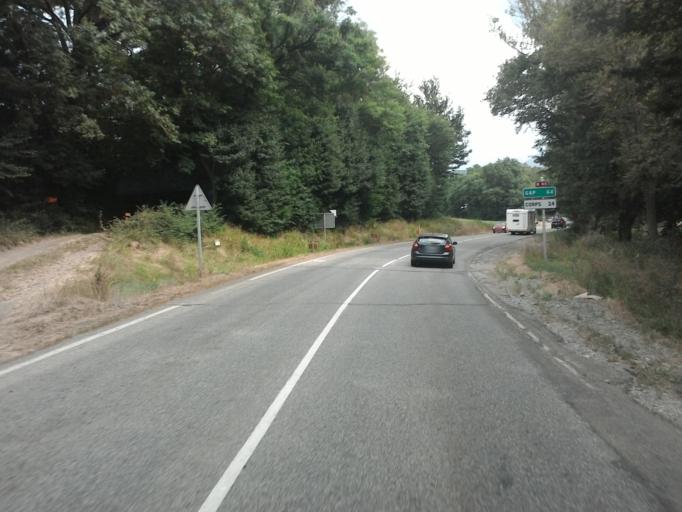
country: FR
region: Rhone-Alpes
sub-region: Departement de l'Isere
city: La Mure
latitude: 44.9010
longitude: 5.8002
